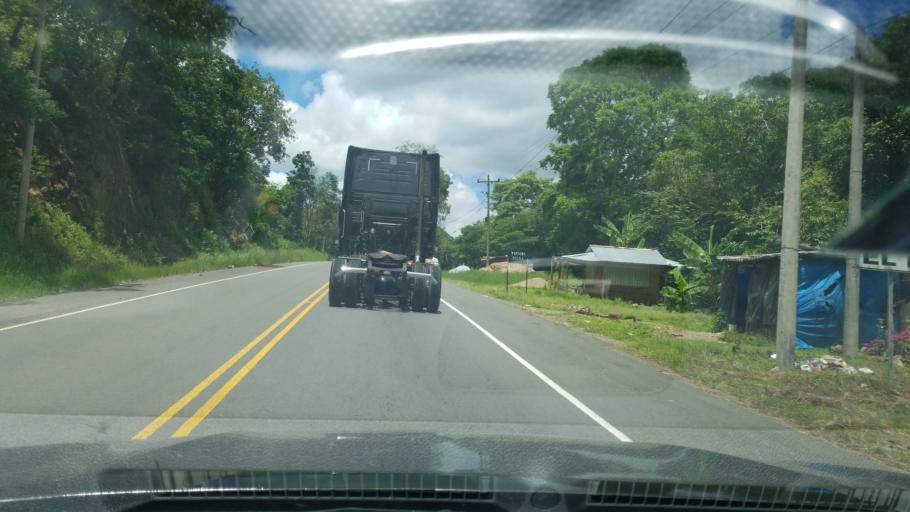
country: HN
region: Francisco Morazan
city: Talanga
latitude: 14.3873
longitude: -87.1346
